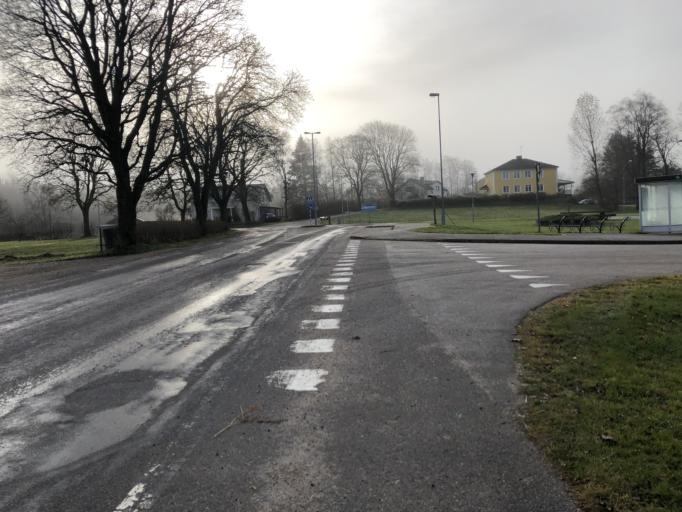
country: SE
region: Vaestra Goetaland
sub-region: Ulricehamns Kommun
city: Ulricehamn
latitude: 57.6947
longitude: 13.5729
